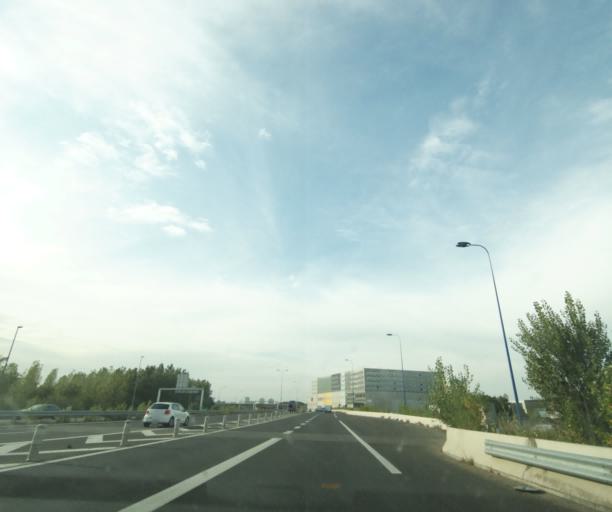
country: FR
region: Midi-Pyrenees
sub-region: Departement de la Haute-Garonne
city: Ramonville-Saint-Agne
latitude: 43.5601
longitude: 1.4897
